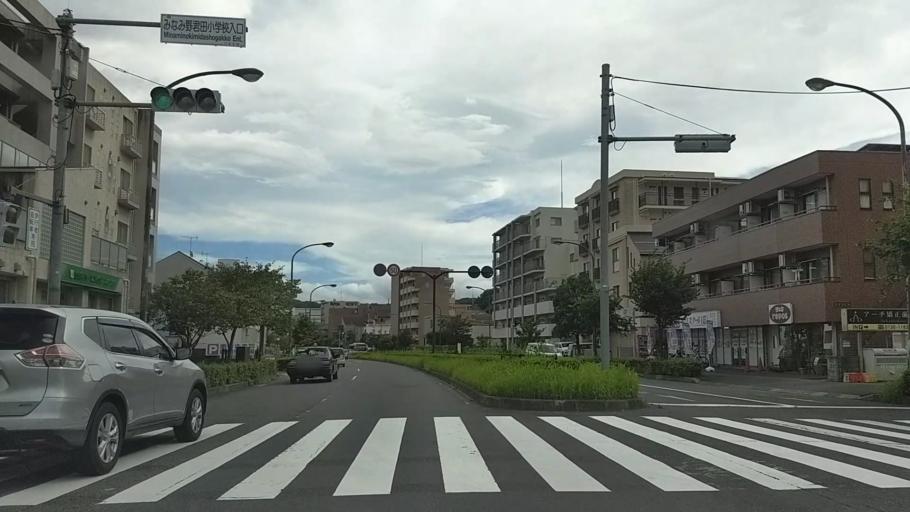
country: JP
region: Tokyo
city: Hachioji
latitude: 35.6278
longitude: 139.3272
